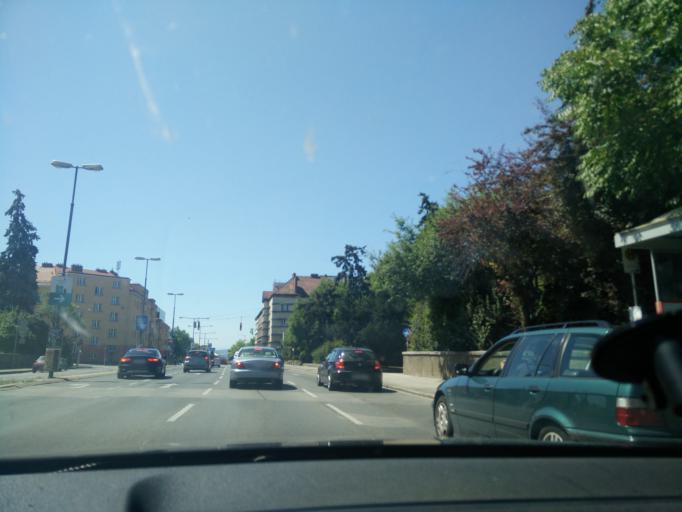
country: AT
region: Vienna
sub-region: Wien Stadt
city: Vienna
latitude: 48.1706
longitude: 16.3499
